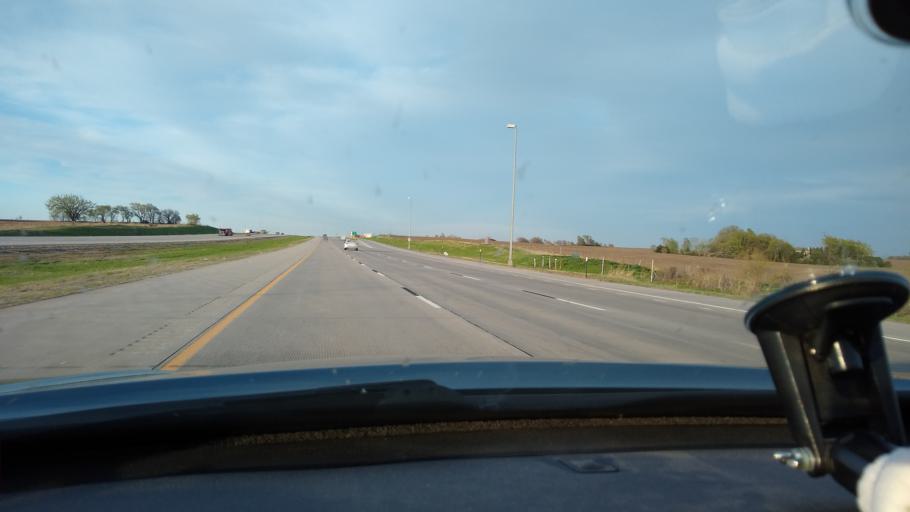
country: US
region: Nebraska
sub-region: Lancaster County
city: Waverly
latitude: 40.9184
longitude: -96.4700
